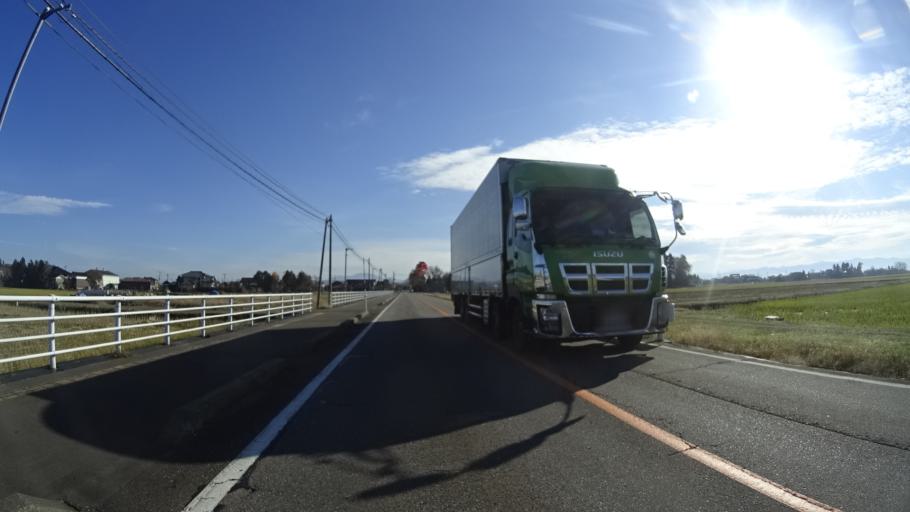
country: JP
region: Niigata
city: Mitsuke
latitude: 37.5549
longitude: 138.8517
